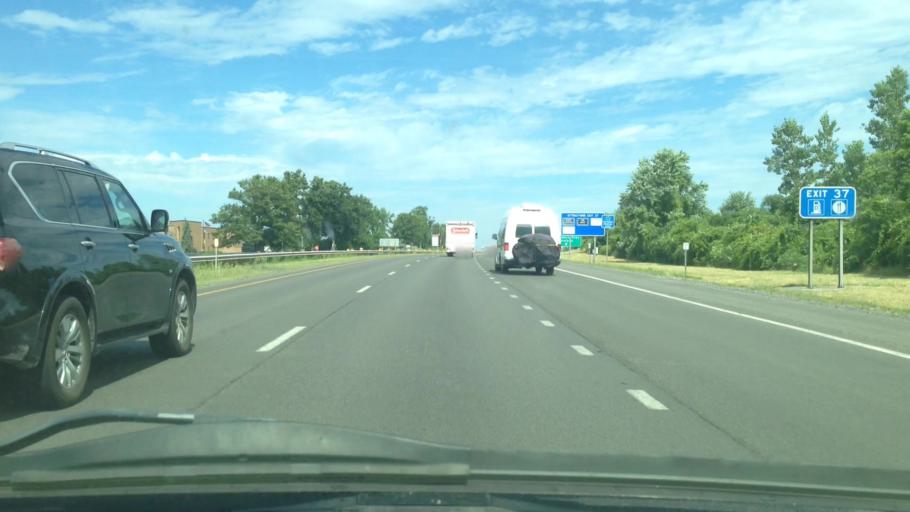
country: US
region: New York
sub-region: Onondaga County
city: Galeville
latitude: 43.0965
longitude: -76.1720
